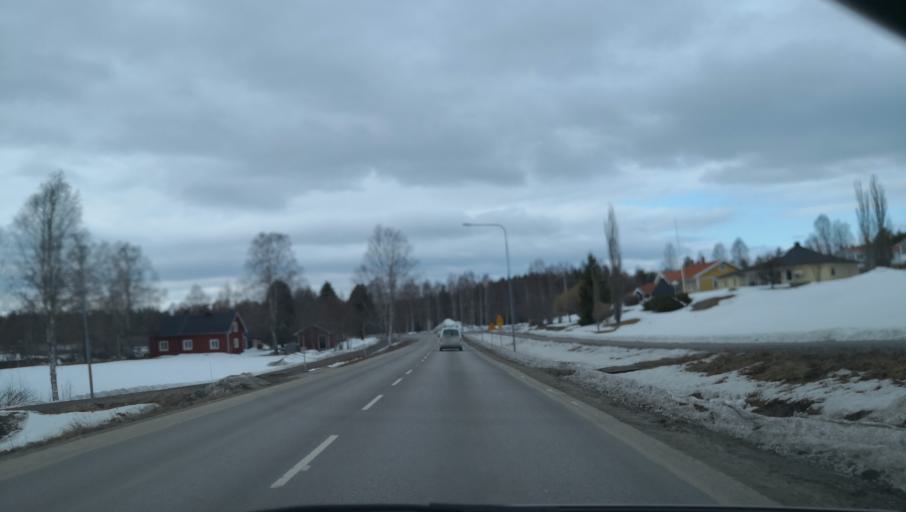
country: SE
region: Vaesterbotten
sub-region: Vannas Kommun
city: Vaennaes
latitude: 63.9185
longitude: 19.7873
